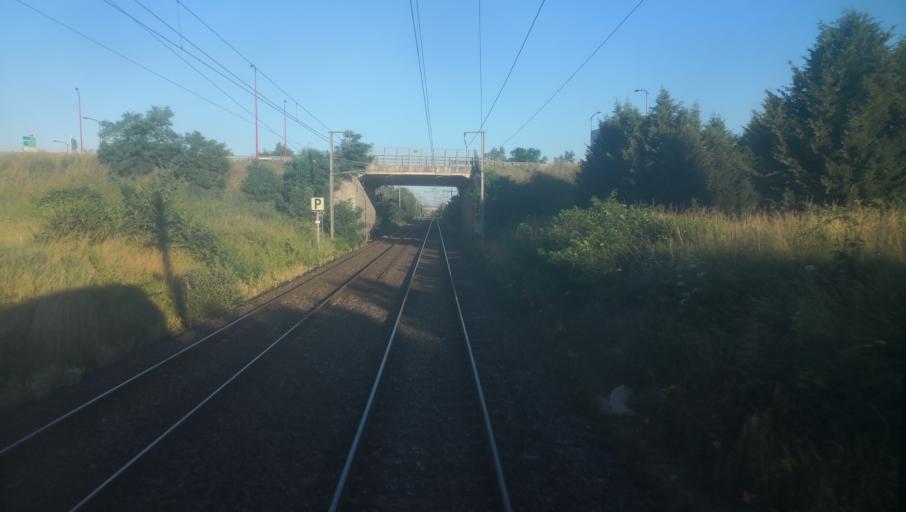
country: FR
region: Auvergne
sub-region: Departement de l'Allier
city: Avermes
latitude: 46.5980
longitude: 3.3065
